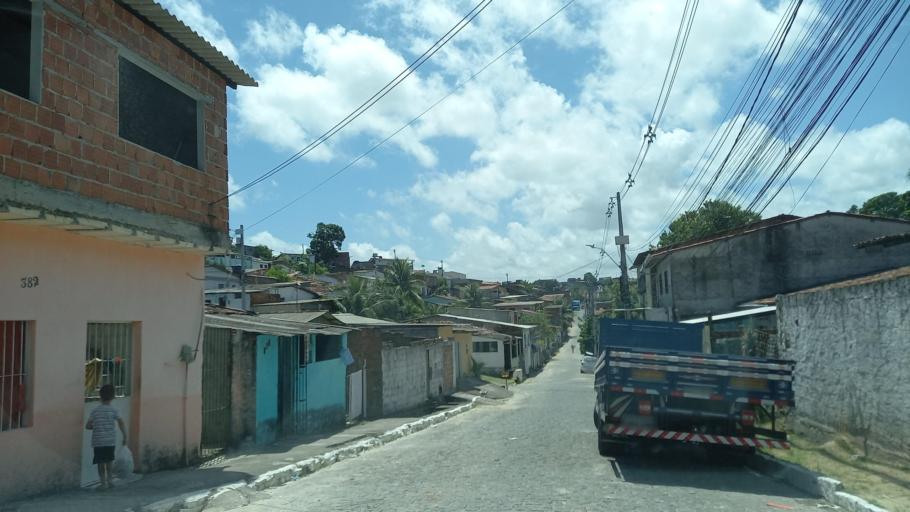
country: BR
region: Pernambuco
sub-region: Jaboatao Dos Guararapes
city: Jaboatao dos Guararapes
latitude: -8.1323
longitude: -34.9547
